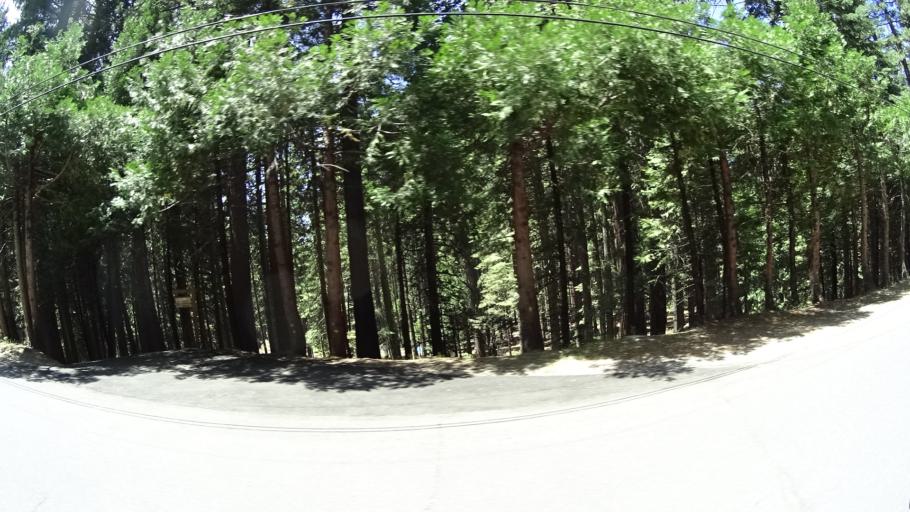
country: US
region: California
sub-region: Calaveras County
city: Arnold
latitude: 38.3002
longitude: -120.2602
